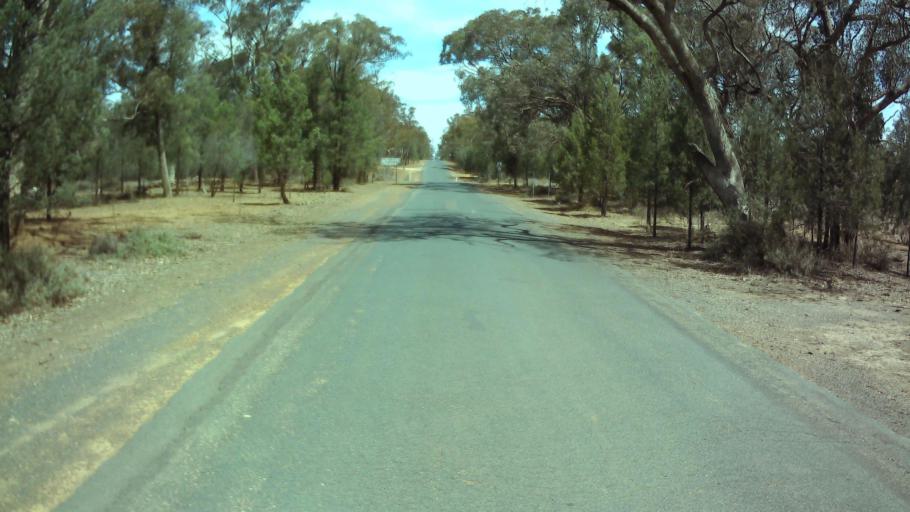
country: AU
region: New South Wales
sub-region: Weddin
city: Grenfell
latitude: -33.8471
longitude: 147.7433
